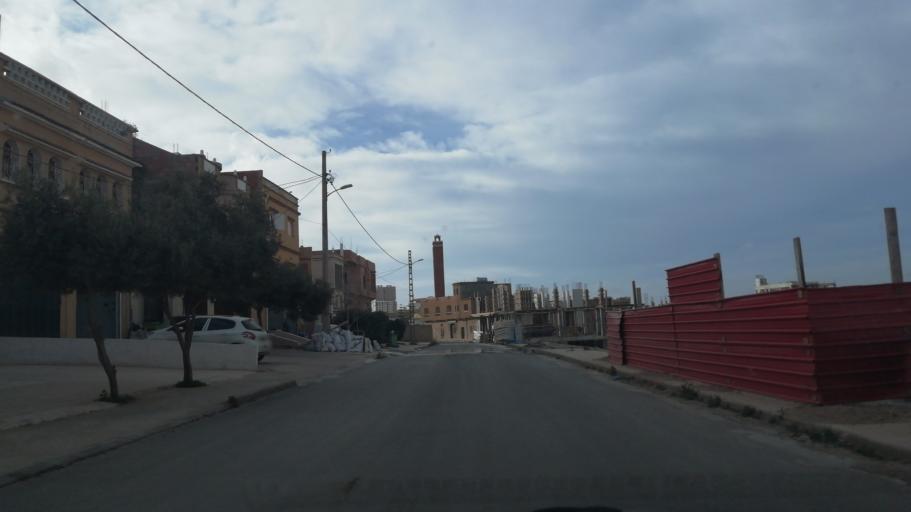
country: DZ
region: Oran
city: Bir el Djir
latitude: 35.7320
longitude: -0.5711
